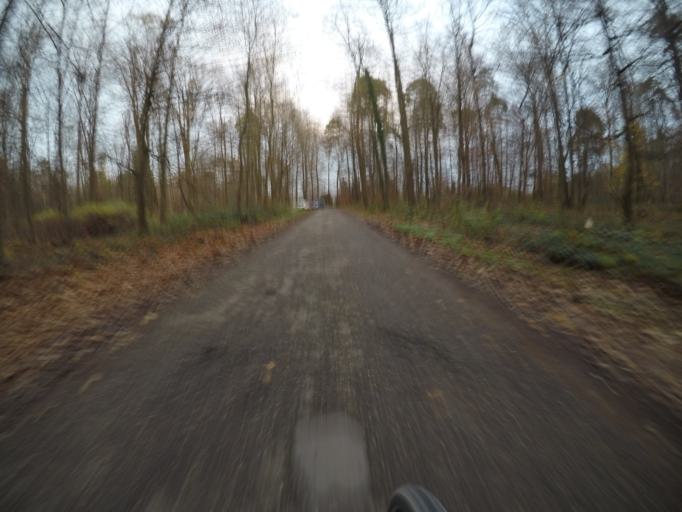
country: DE
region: Baden-Wuerttemberg
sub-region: Regierungsbezirk Stuttgart
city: Ostfildern
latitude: 48.7455
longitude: 9.2535
